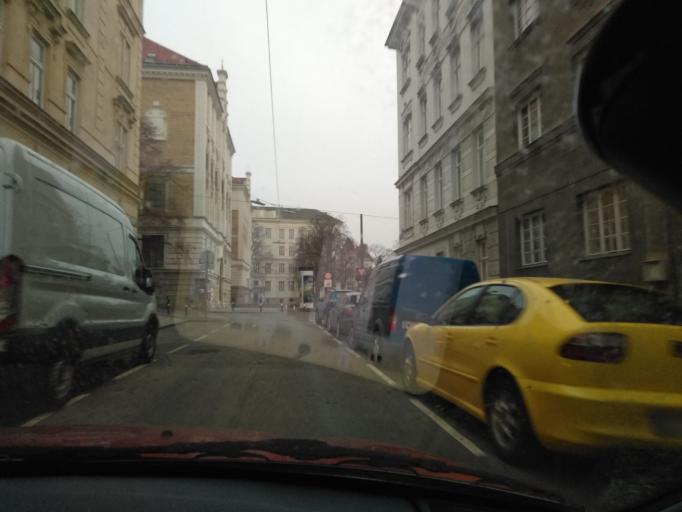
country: AT
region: Vienna
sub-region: Wien Stadt
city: Vienna
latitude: 48.2260
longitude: 16.3358
